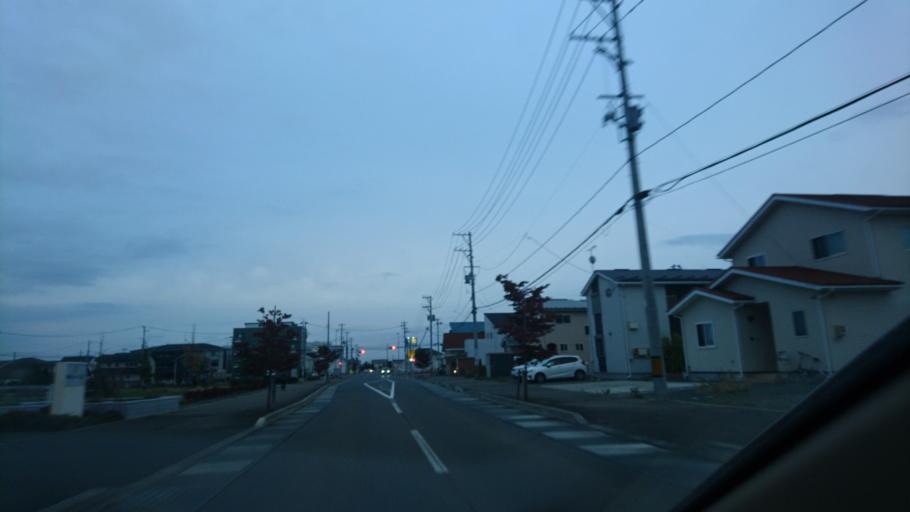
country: JP
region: Iwate
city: Morioka-shi
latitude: 39.6739
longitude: 141.1321
